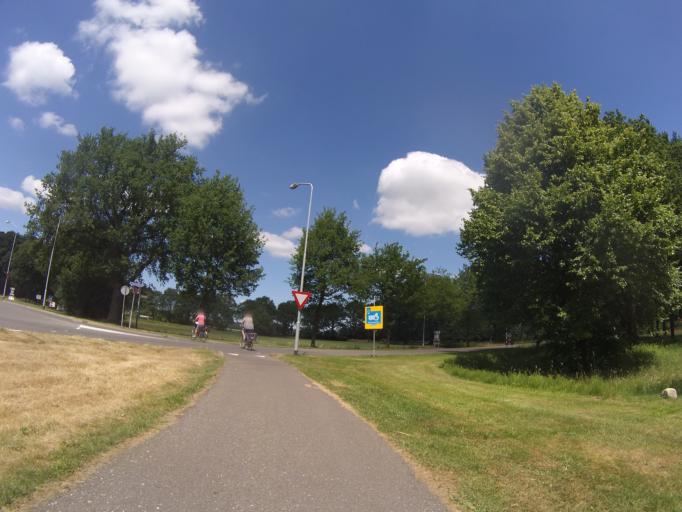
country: NL
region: Drenthe
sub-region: Gemeente Emmen
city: Emmen
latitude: 52.8422
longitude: 6.8794
